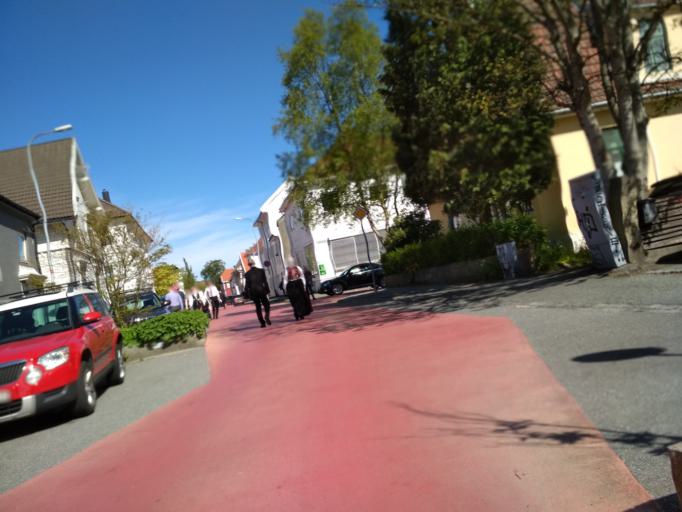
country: NO
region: Rogaland
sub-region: Stavanger
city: Stavanger
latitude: 58.9678
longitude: 5.7254
